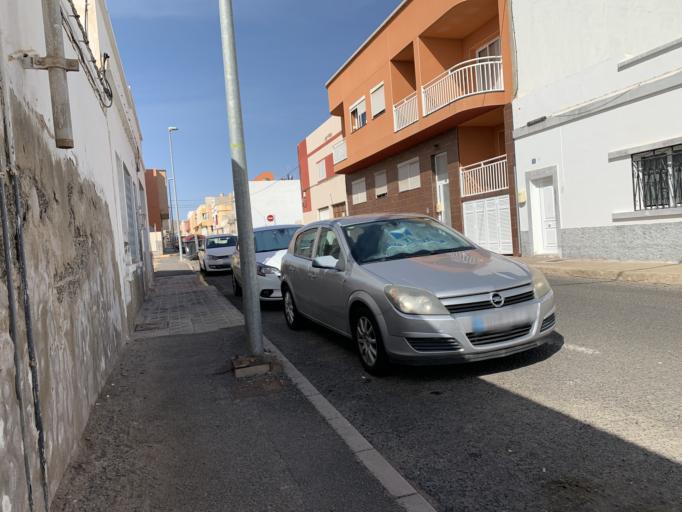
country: ES
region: Canary Islands
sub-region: Provincia de Las Palmas
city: Puerto del Rosario
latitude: 28.4990
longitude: -13.8671
